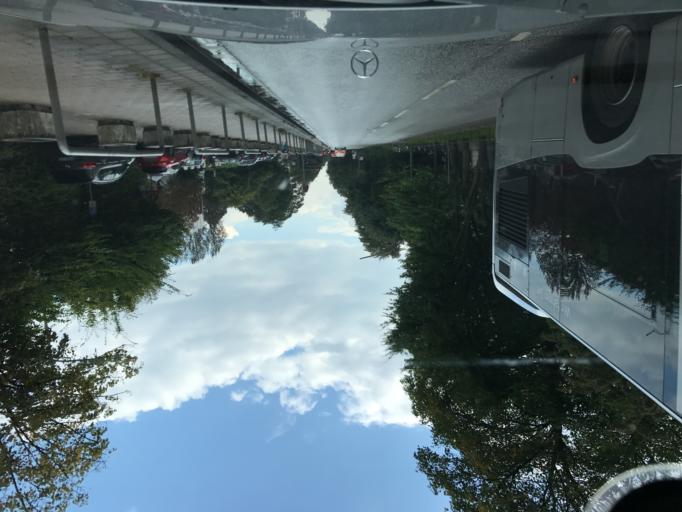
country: DE
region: Hamburg
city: Eimsbuettel
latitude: 53.5728
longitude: 9.9920
